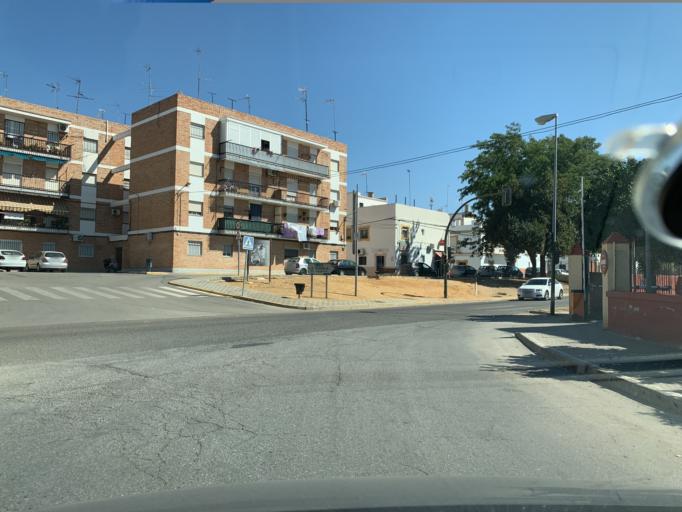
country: ES
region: Andalusia
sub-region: Provincia de Sevilla
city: Marchena
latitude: 37.3284
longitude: -5.4088
